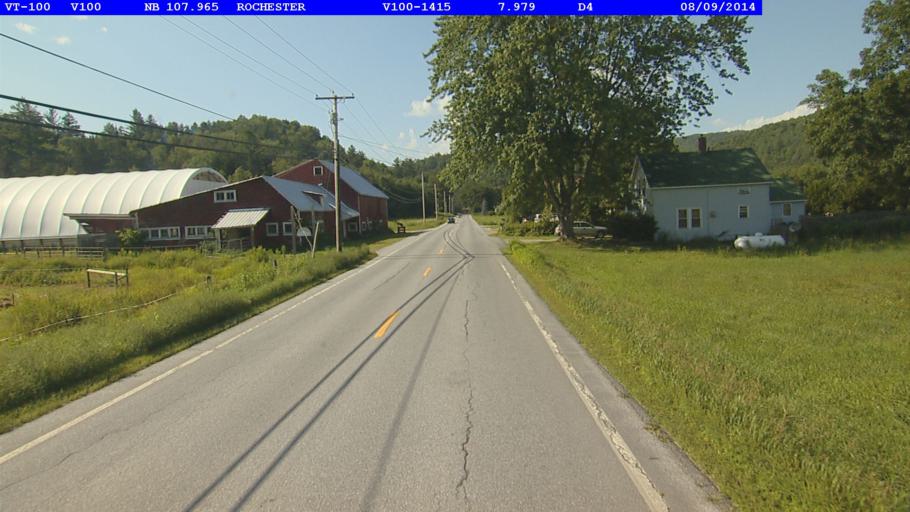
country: US
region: Vermont
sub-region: Orange County
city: Randolph
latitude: 43.9076
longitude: -72.8295
